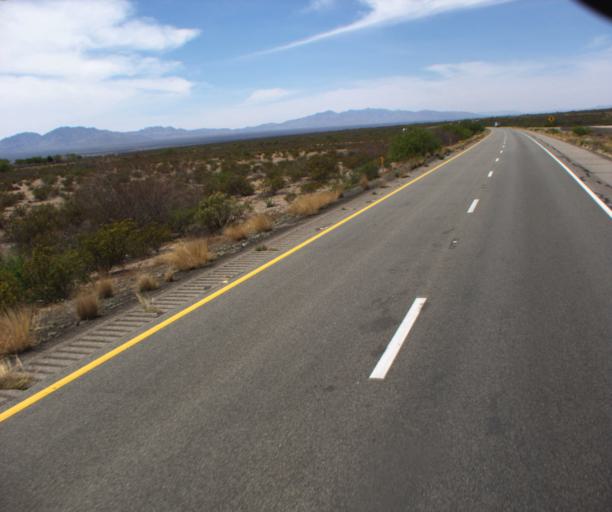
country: US
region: New Mexico
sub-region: Hidalgo County
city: Lordsburg
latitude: 32.2383
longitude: -109.0864
